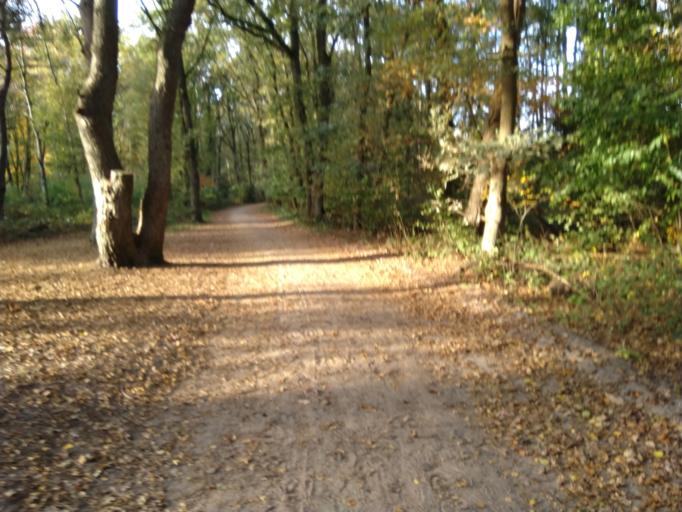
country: NL
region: Drenthe
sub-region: Gemeente Tynaarlo
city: Zuidlaren
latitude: 53.0722
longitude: 6.6592
